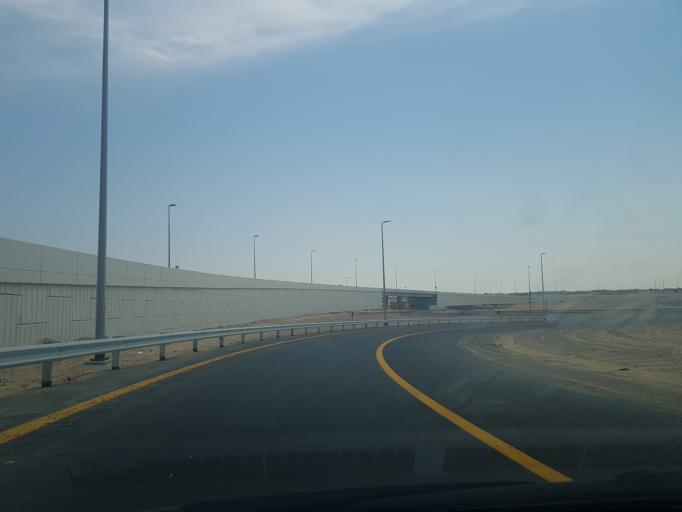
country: AE
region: Ash Shariqah
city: Sharjah
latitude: 25.2394
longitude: 55.5688
